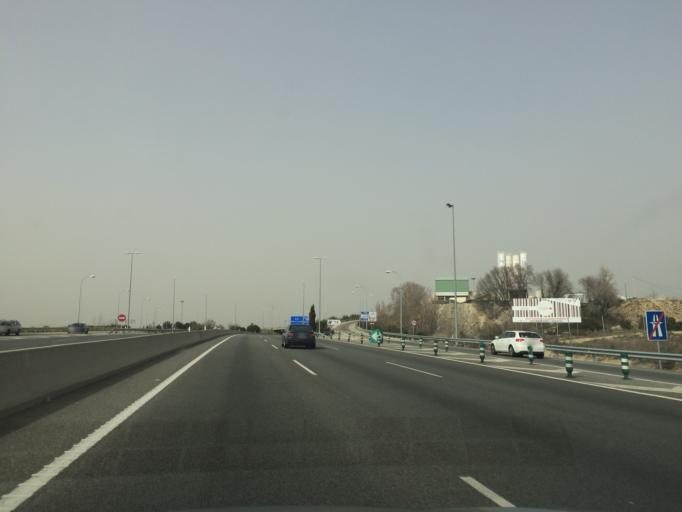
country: ES
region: Madrid
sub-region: Provincia de Madrid
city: Majadahonda
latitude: 40.4754
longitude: -3.8952
